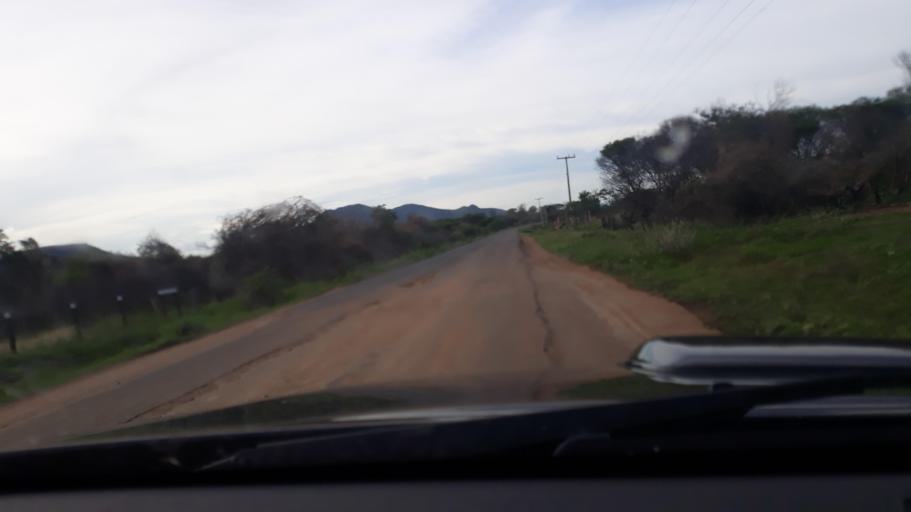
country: BR
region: Bahia
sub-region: Guanambi
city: Guanambi
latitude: -14.0048
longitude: -42.8586
